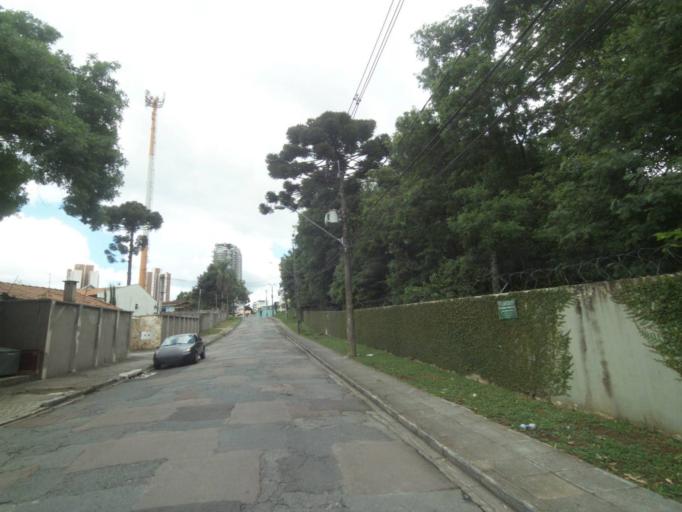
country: BR
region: Parana
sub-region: Curitiba
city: Curitiba
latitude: -25.4354
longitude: -49.3401
